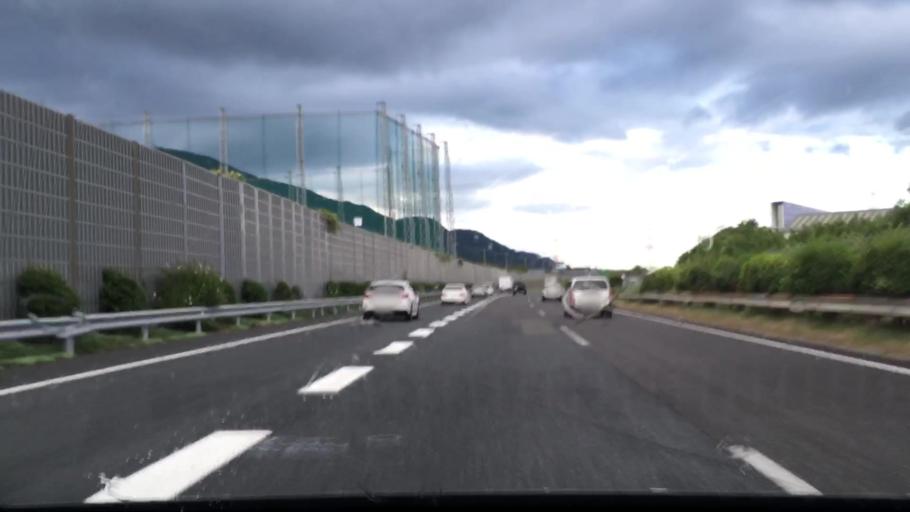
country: JP
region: Fukuoka
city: Kitakyushu
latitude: 33.8286
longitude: 130.8999
